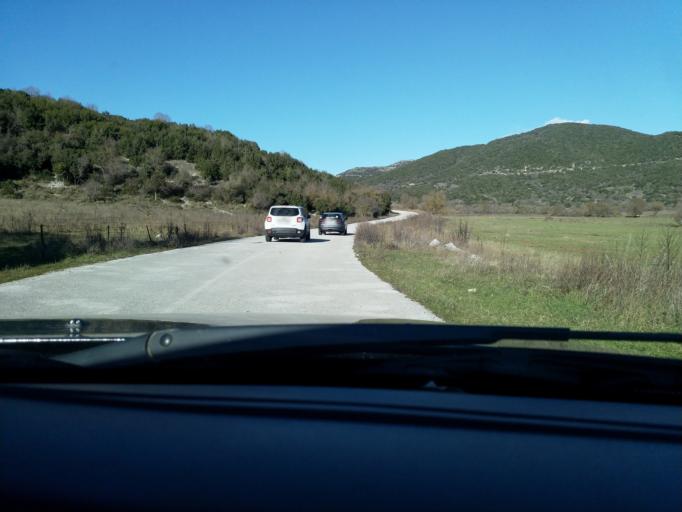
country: GR
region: Epirus
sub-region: Nomos Ioanninon
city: Kalpaki
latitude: 39.8862
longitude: 20.6729
